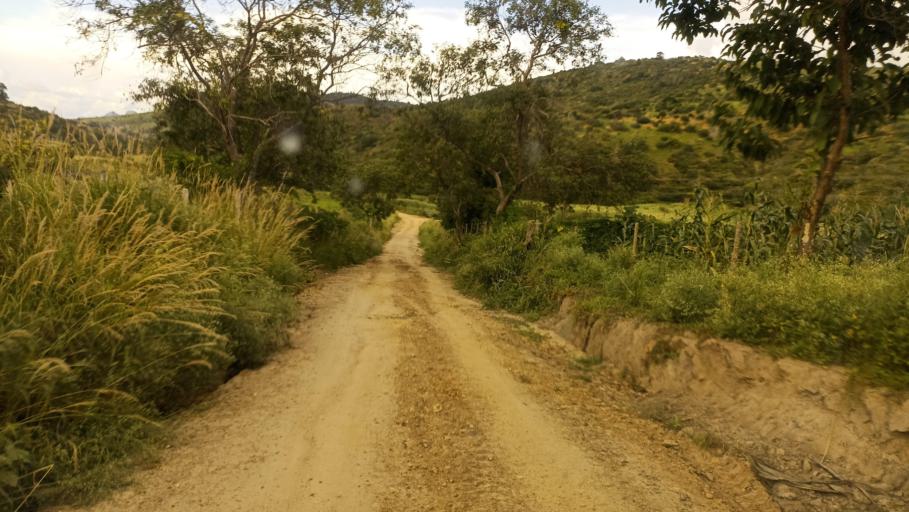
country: BR
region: Minas Gerais
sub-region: Almenara
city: Almenara
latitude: -16.5367
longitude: -40.4415
